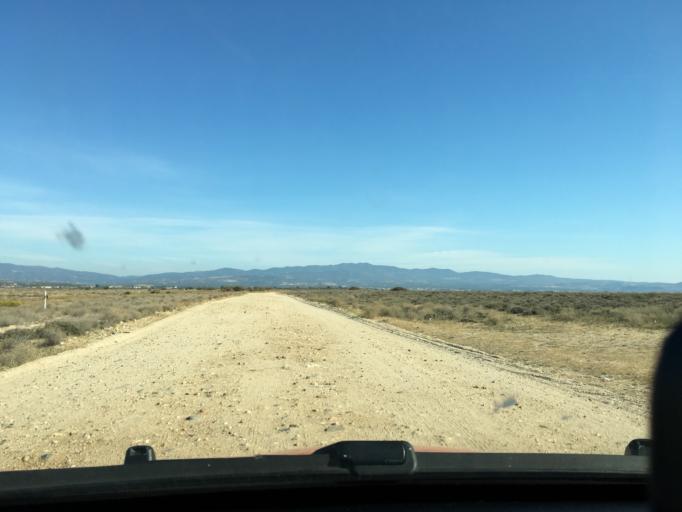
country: GR
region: Central Macedonia
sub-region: Nomos Chalkidikis
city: Nea Potidhaia
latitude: 40.2246
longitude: 23.3365
